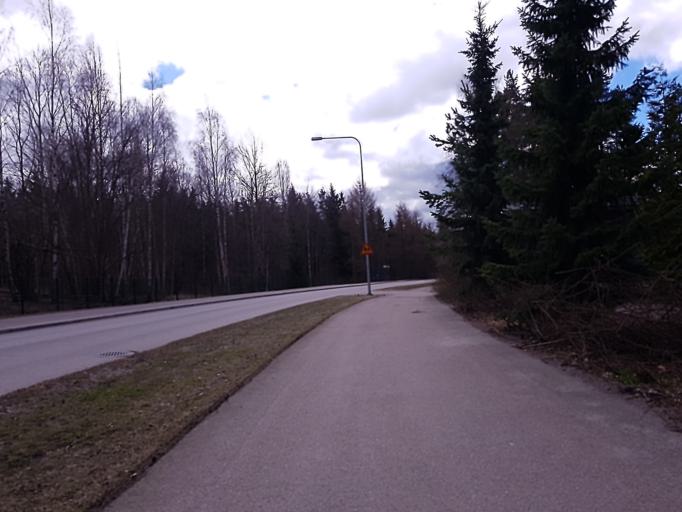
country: FI
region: Uusimaa
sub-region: Helsinki
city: Helsinki
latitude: 60.2396
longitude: 24.9025
